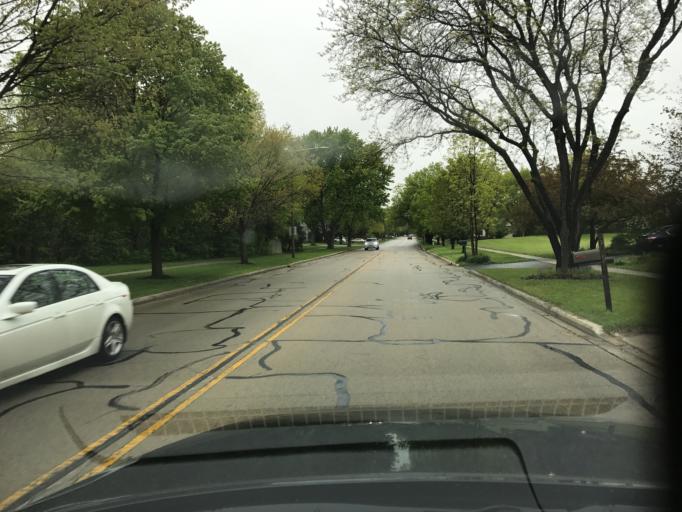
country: US
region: Illinois
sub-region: DuPage County
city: Naperville
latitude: 41.7630
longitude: -88.1243
